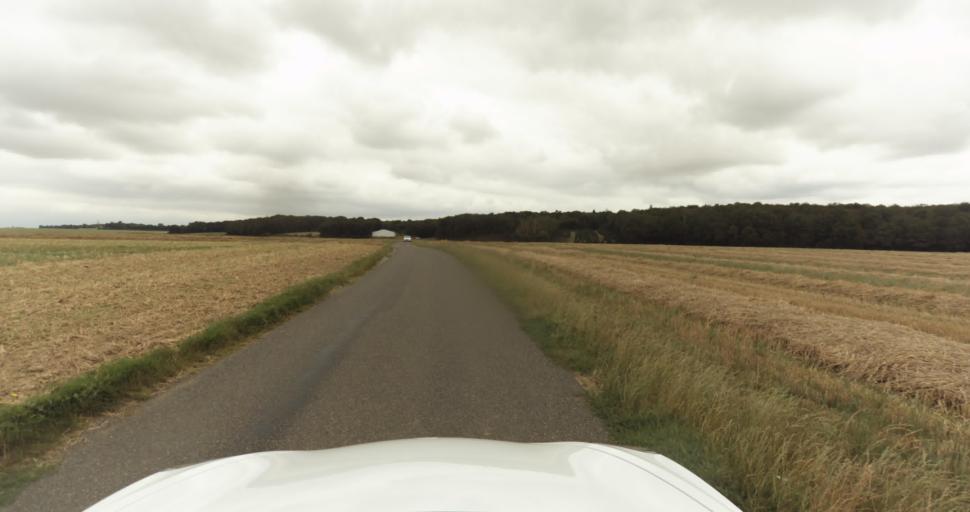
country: FR
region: Haute-Normandie
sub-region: Departement de l'Eure
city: Saint-Sebastien-de-Morsent
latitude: 49.0270
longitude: 1.0619
